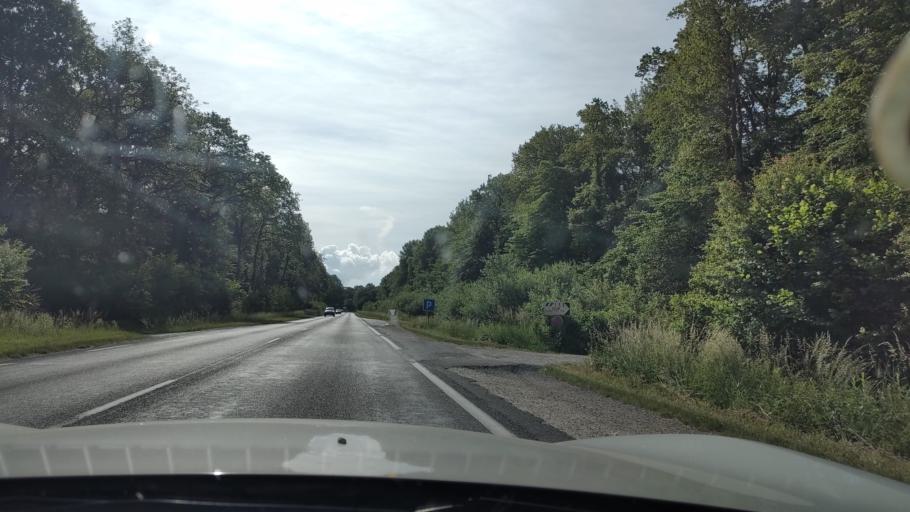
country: FR
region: Ile-de-France
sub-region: Departement de Seine-et-Marne
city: Sourdun
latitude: 48.5297
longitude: 3.3965
